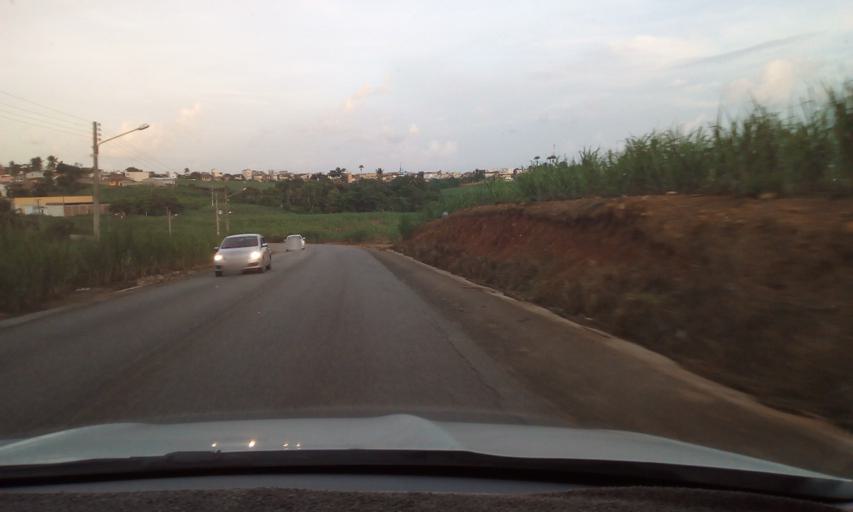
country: BR
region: Pernambuco
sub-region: Vicencia
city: Vicencia
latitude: -7.6004
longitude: -35.2386
